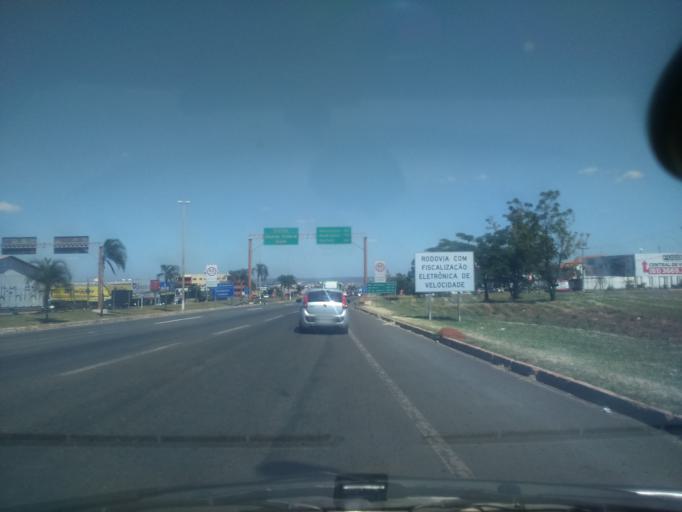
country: BR
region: Goias
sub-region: Luziania
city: Luziania
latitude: -16.0506
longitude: -47.9817
